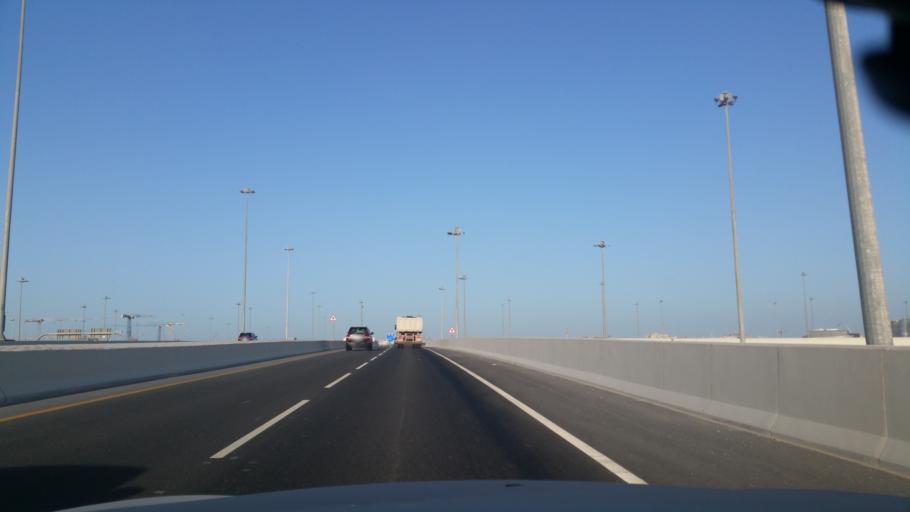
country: QA
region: Baladiyat Umm Salal
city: Umm Salal Muhammad
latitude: 25.4027
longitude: 51.4883
